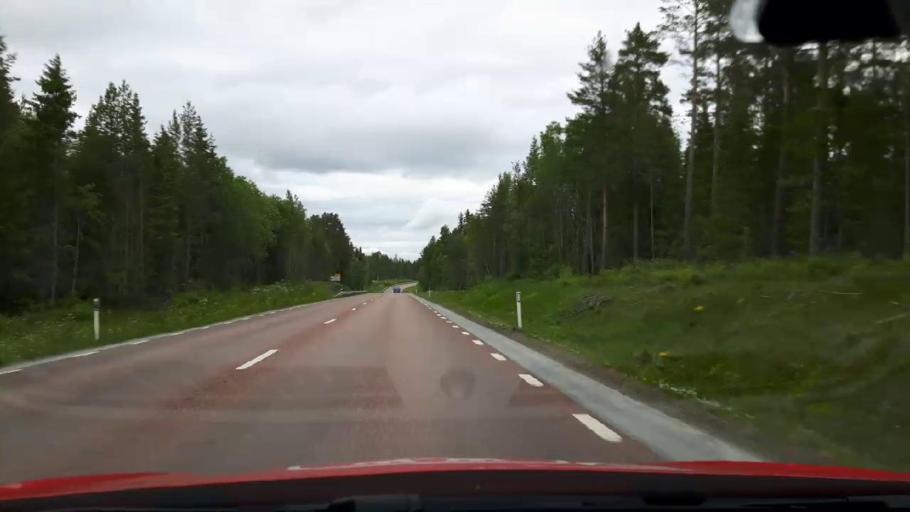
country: SE
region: Jaemtland
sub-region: Bergs Kommun
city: Hoverberg
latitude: 62.9460
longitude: 14.5438
